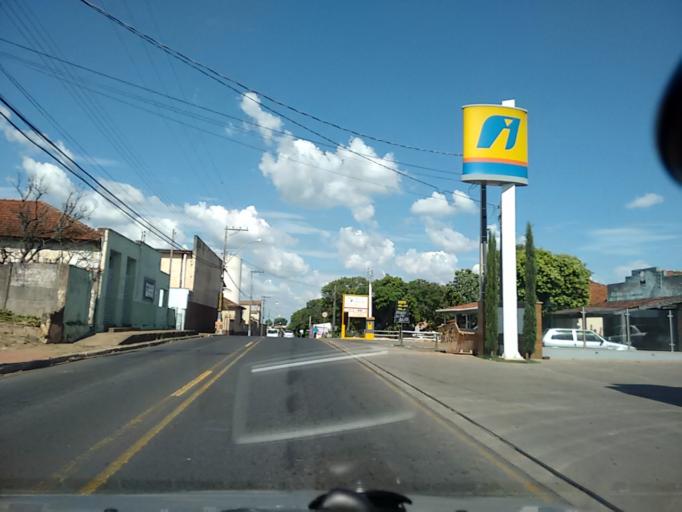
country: BR
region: Sao Paulo
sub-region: Pompeia
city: Pompeia
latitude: -22.1030
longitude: -50.1868
